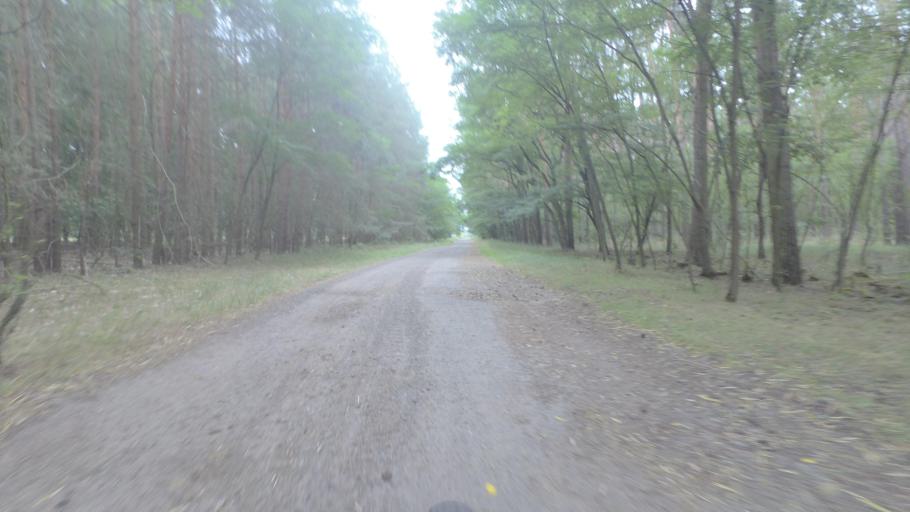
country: DE
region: Brandenburg
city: Rangsdorf
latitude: 52.2639
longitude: 13.3963
